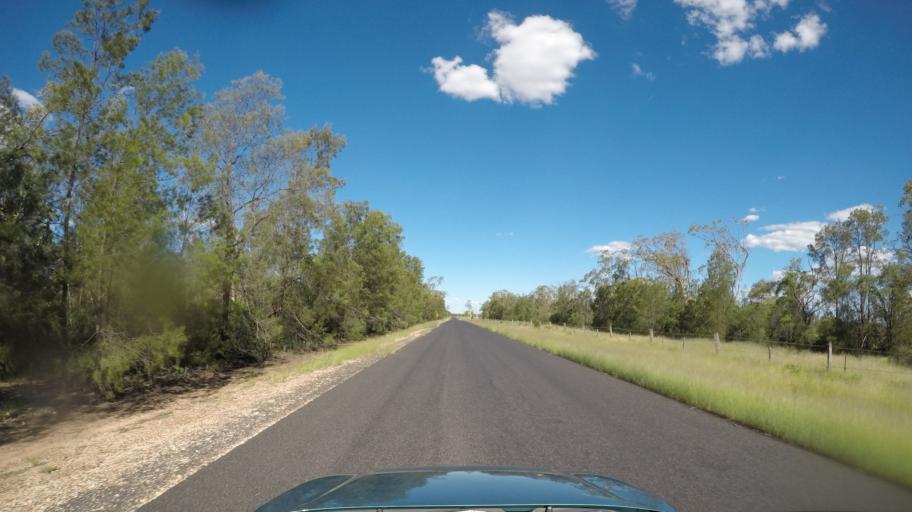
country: AU
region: Queensland
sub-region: Goondiwindi
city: Goondiwindi
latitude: -28.1675
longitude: 150.4511
